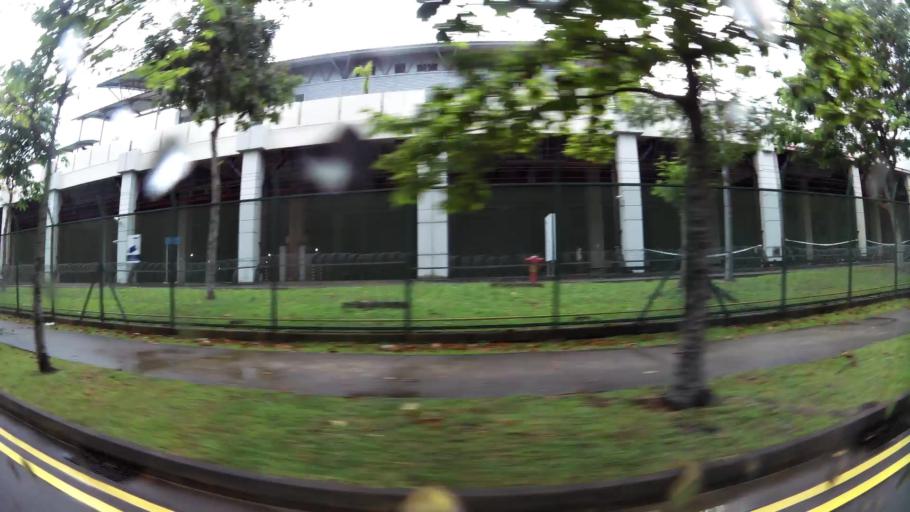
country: MY
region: Johor
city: Kampung Pasir Gudang Baru
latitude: 1.3904
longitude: 103.8840
